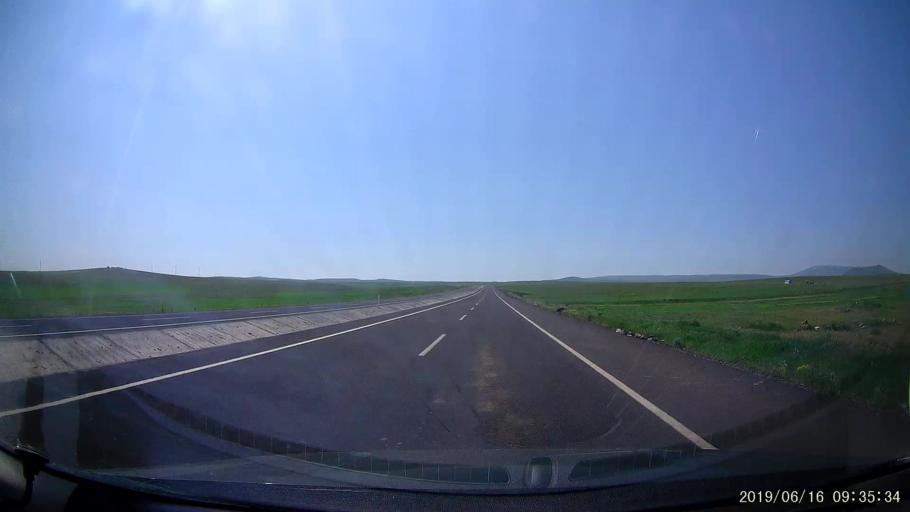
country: TR
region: Kars
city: Kars
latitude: 40.5698
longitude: 43.1580
